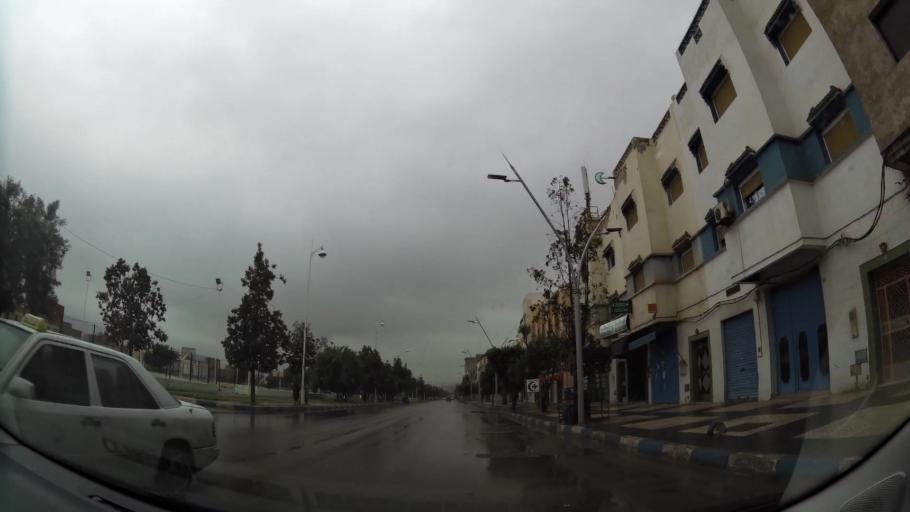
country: MA
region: Oriental
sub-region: Nador
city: Nador
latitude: 35.1658
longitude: -2.9531
